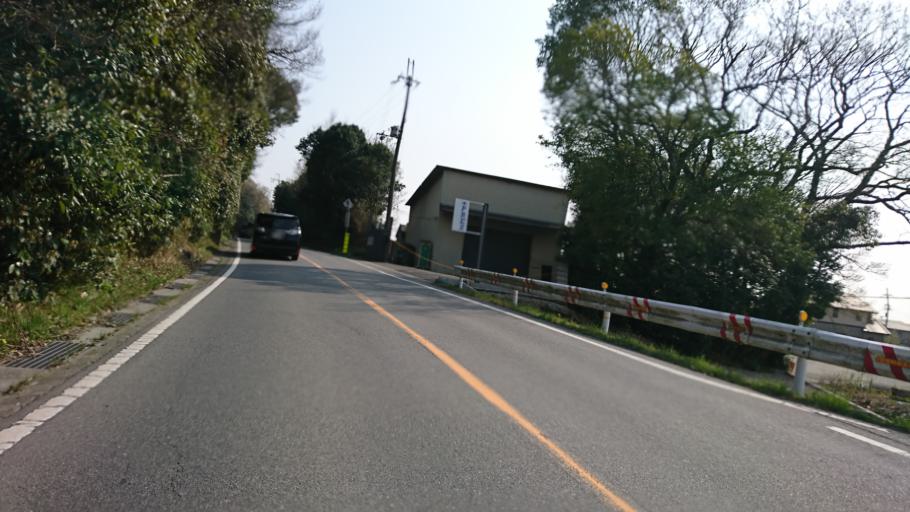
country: JP
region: Hyogo
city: Ono
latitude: 34.8039
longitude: 134.9250
